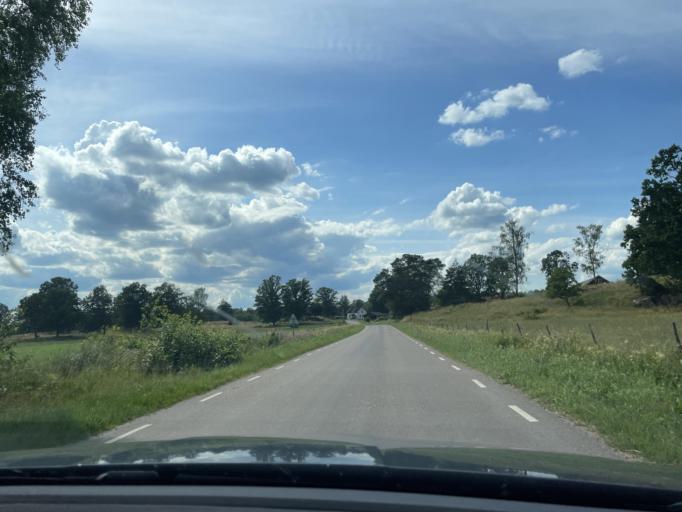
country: SE
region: Kalmar
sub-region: Vimmerby Kommun
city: Sodra Vi
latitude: 57.8158
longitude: 15.7624
